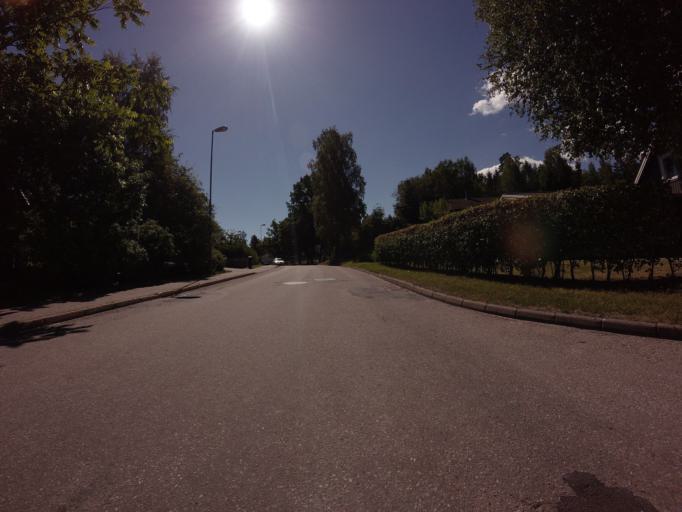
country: SE
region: Stockholm
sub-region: Sollentuna Kommun
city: Sollentuna
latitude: 59.4550
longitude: 17.8944
